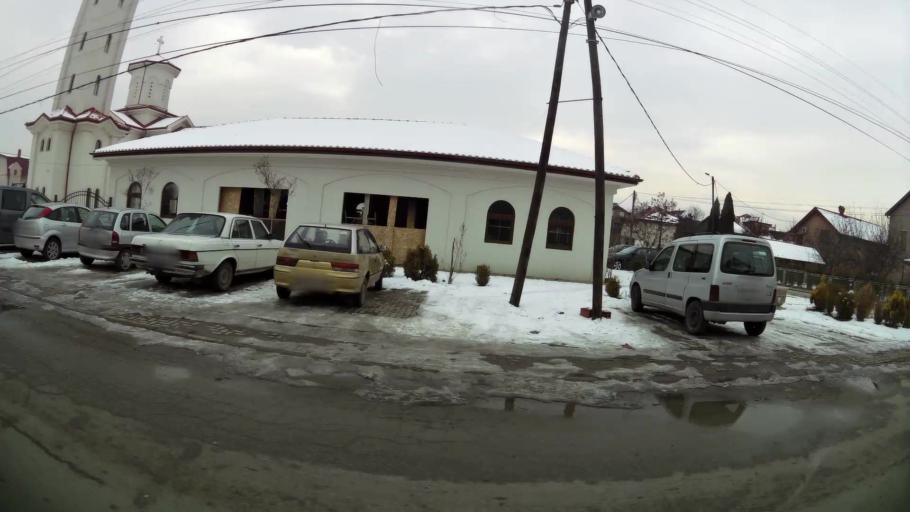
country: MK
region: Butel
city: Butel
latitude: 42.0390
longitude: 21.4469
